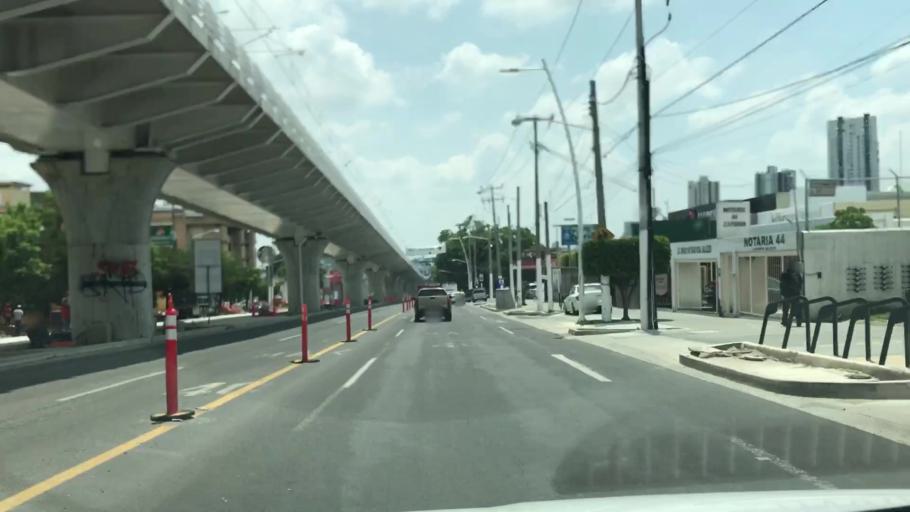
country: MX
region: Jalisco
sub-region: Zapopan
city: Zapopan
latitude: 20.7183
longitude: -103.3845
